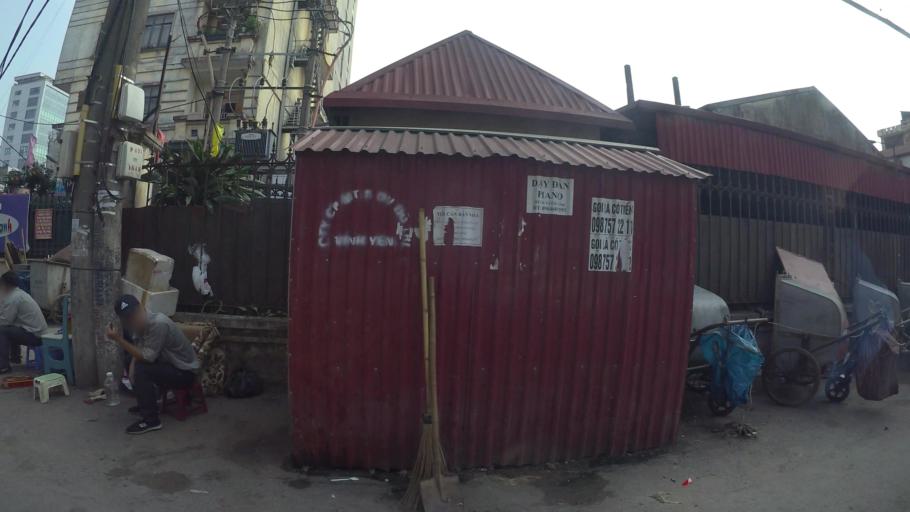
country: VN
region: Ha Noi
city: Tay Ho
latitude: 21.0510
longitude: 105.8071
